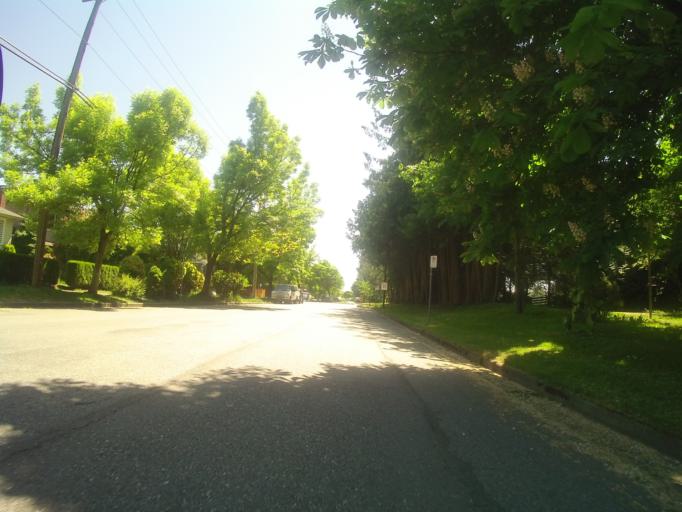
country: CA
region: British Columbia
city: Vancouver
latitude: 49.2218
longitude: -123.1062
